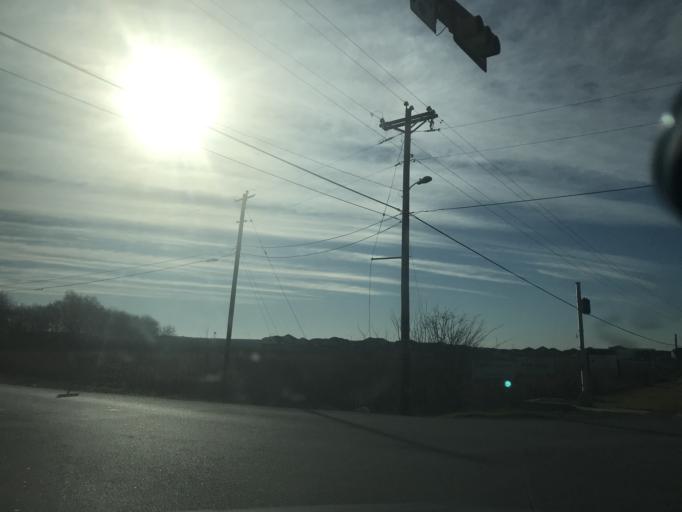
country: US
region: Texas
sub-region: Travis County
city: Manor
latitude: 30.3378
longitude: -97.5585
